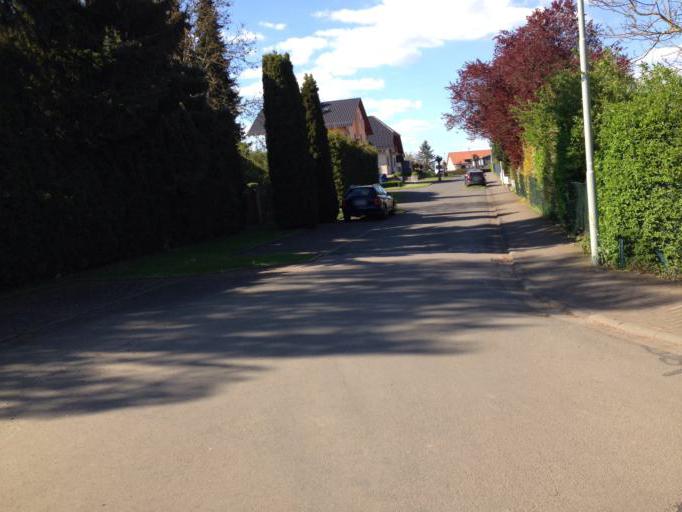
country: DE
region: Hesse
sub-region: Regierungsbezirk Giessen
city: Grunberg
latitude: 50.5584
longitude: 8.8989
